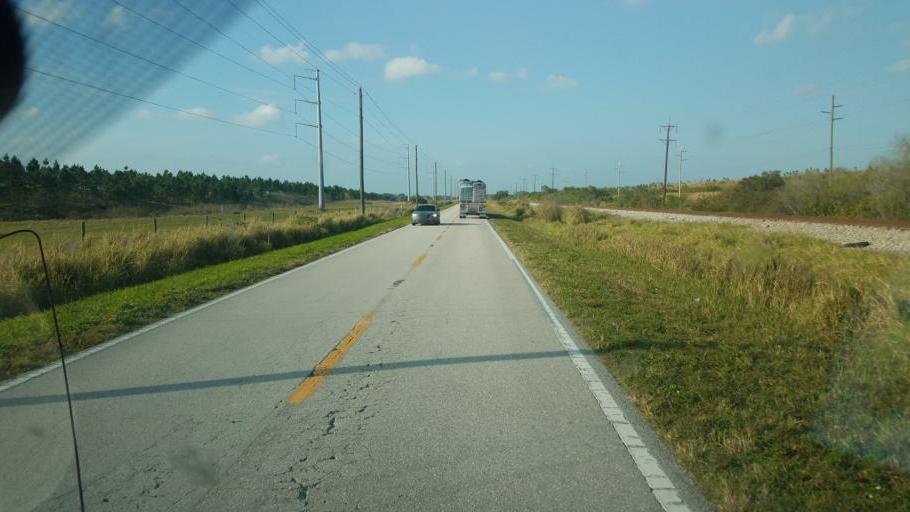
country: US
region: Florida
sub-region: Hardee County
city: Bowling Green
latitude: 27.7073
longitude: -81.9597
